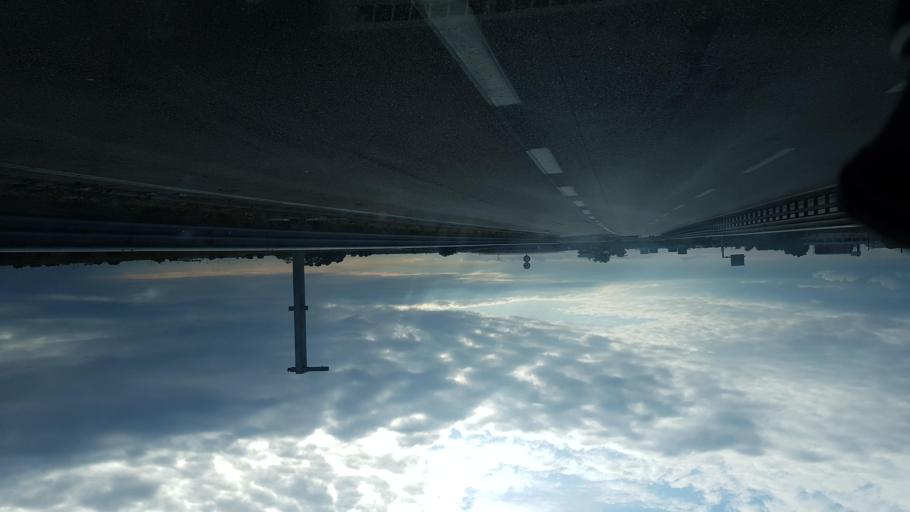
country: IT
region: Apulia
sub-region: Provincia di Brindisi
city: Francavilla Fontana
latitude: 40.5388
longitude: 17.5336
